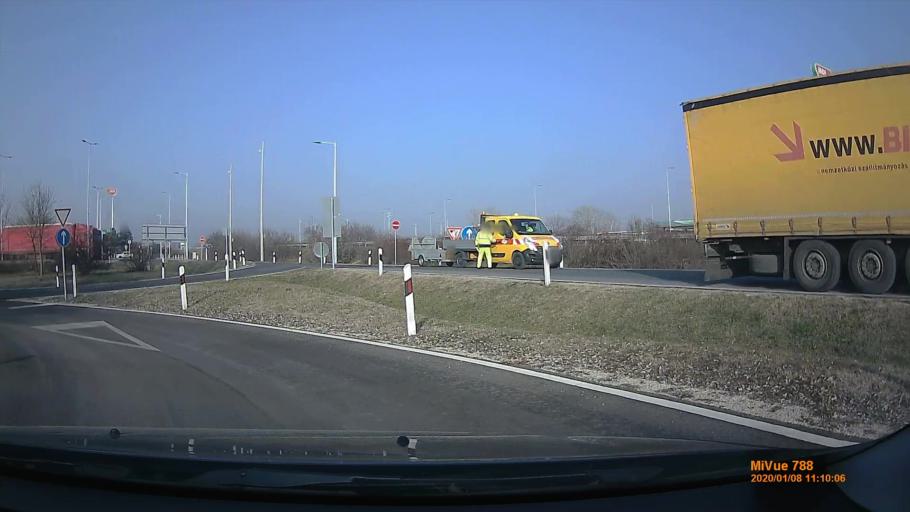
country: HU
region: Bacs-Kiskun
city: Helvecia
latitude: 46.8467
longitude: 19.6663
